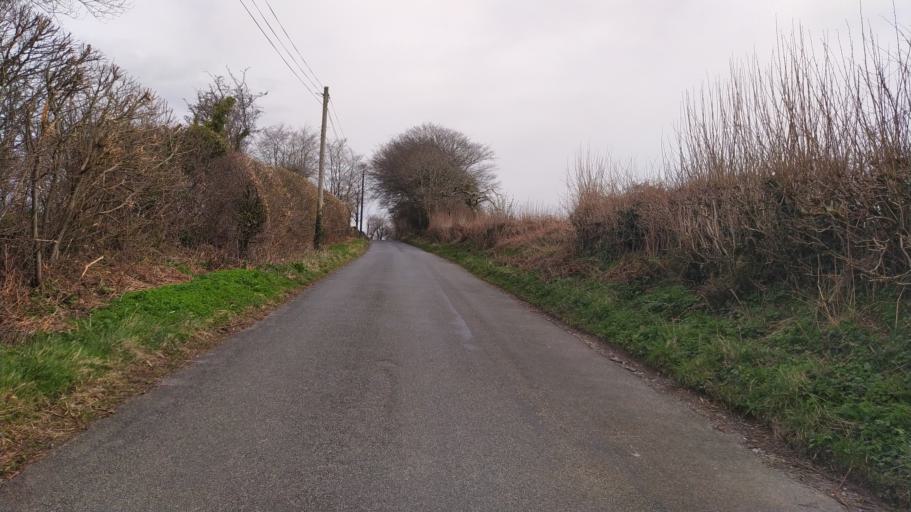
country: GB
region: England
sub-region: Dorset
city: Beaminster
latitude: 50.8319
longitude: -2.7073
